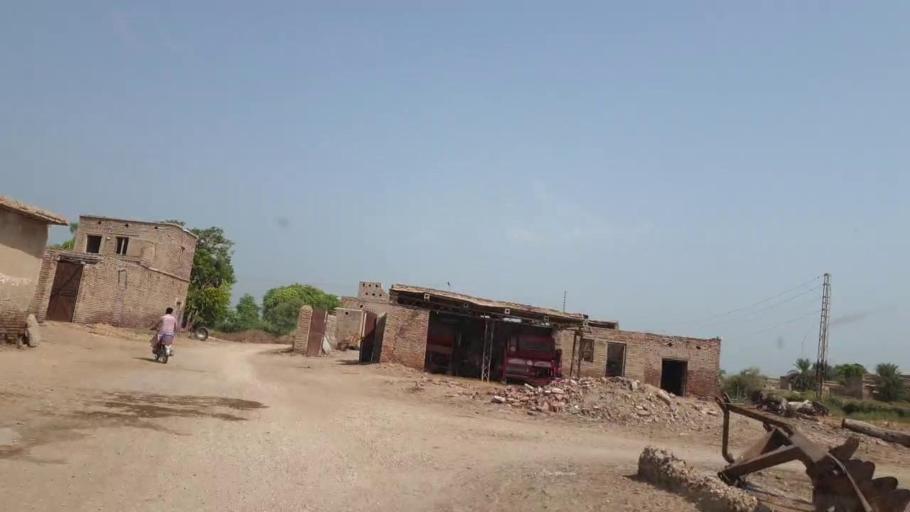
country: PK
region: Sindh
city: Lakhi
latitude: 27.8719
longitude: 68.6599
